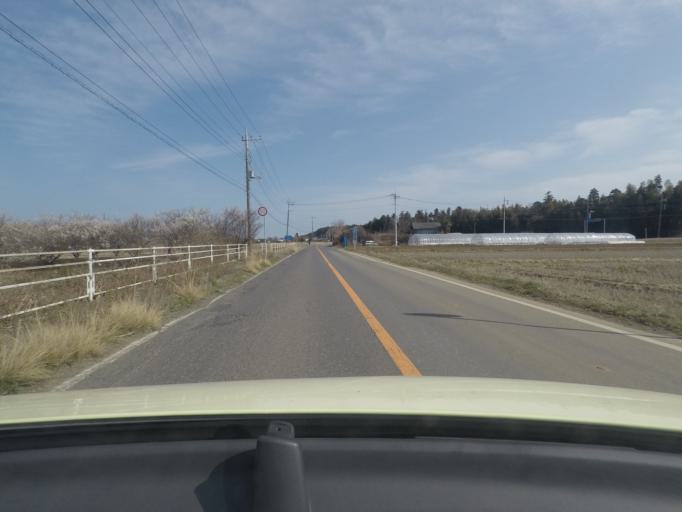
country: JP
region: Ibaraki
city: Okunoya
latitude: 36.2674
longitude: 140.4926
